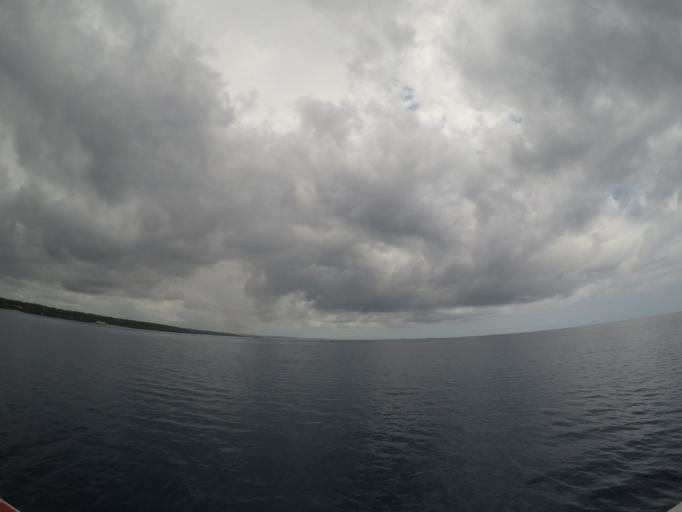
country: TZ
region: Zanzibar North
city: Mkokotoni
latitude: -5.9836
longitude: 39.1734
